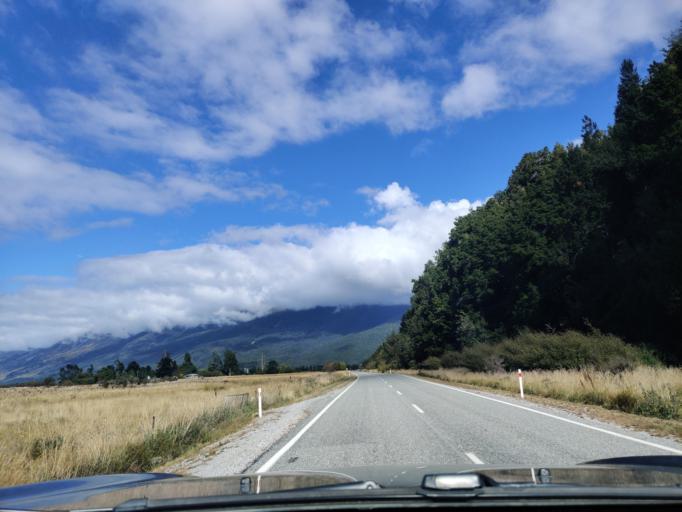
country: NZ
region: Otago
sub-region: Queenstown-Lakes District
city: Queenstown
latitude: -44.7958
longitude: 168.3801
